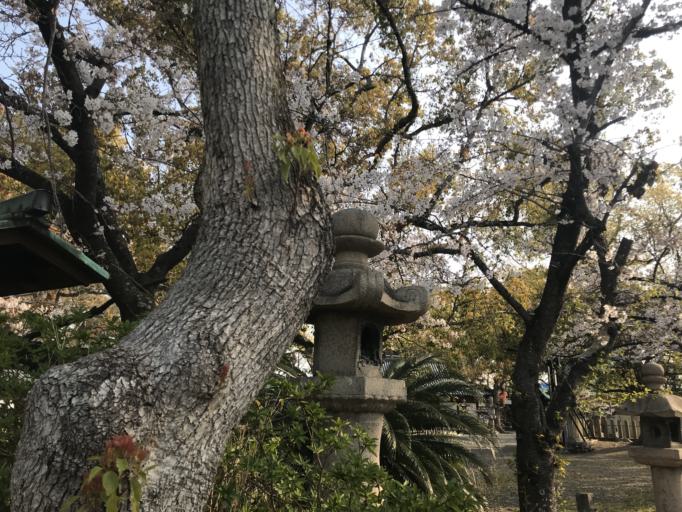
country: JP
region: Osaka
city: Izumi
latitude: 34.4961
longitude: 135.4193
